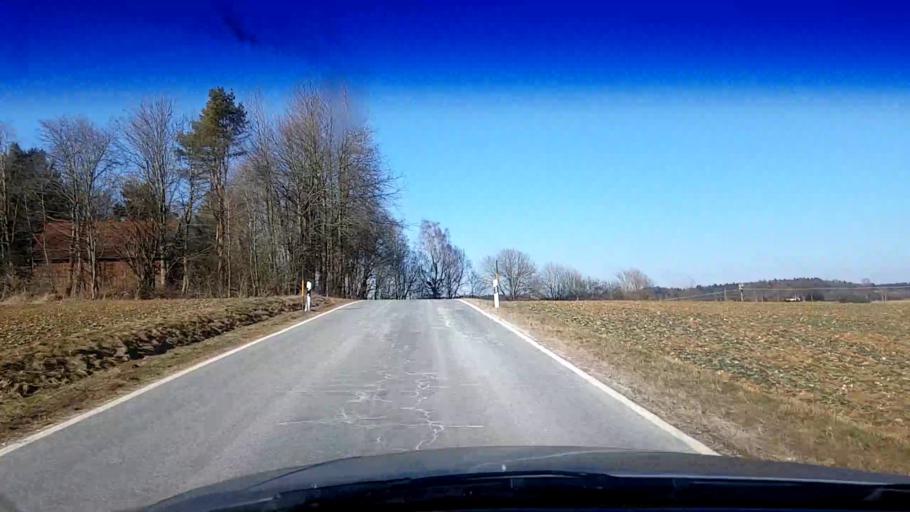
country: DE
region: Bavaria
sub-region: Upper Franconia
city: Aufsess
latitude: 49.9228
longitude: 11.2188
